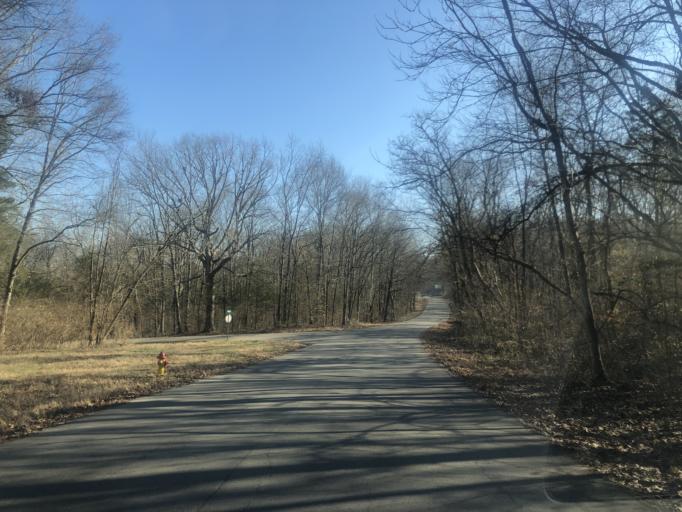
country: US
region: Tennessee
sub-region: Rutherford County
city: La Vergne
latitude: 36.0087
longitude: -86.5881
